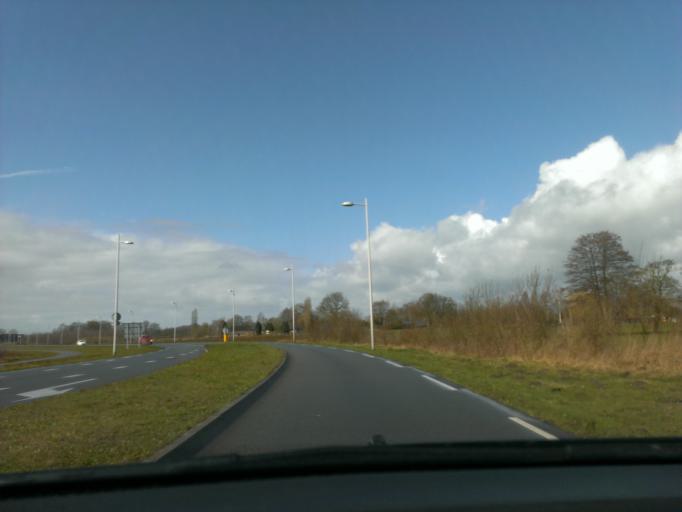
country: NL
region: Gelderland
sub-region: Gemeente Apeldoorn
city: Apeldoorn
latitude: 52.2468
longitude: 5.9880
